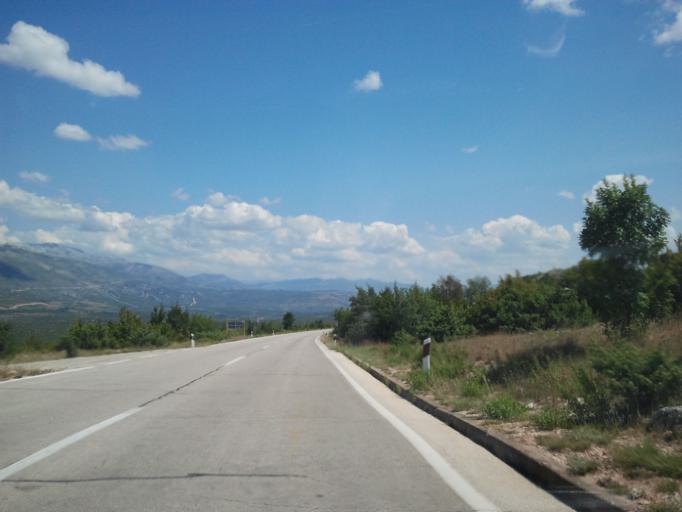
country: HR
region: Zadarska
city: Krusevo
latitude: 44.1973
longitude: 15.6592
